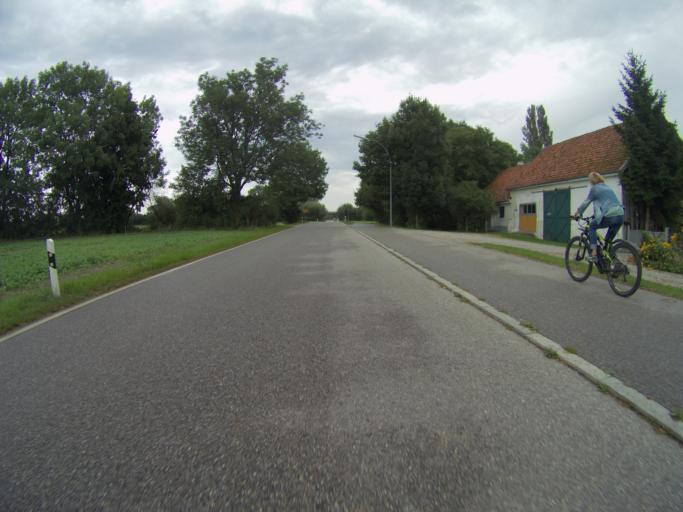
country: DE
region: Bavaria
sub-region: Upper Bavaria
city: Marzling
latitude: 48.3901
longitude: 11.7746
